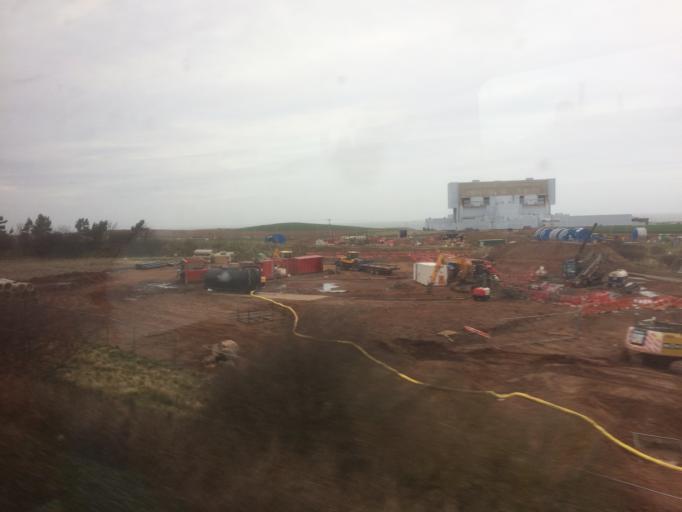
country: GB
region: Scotland
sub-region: East Lothian
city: Dunbar
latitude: 55.9604
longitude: -2.4129
